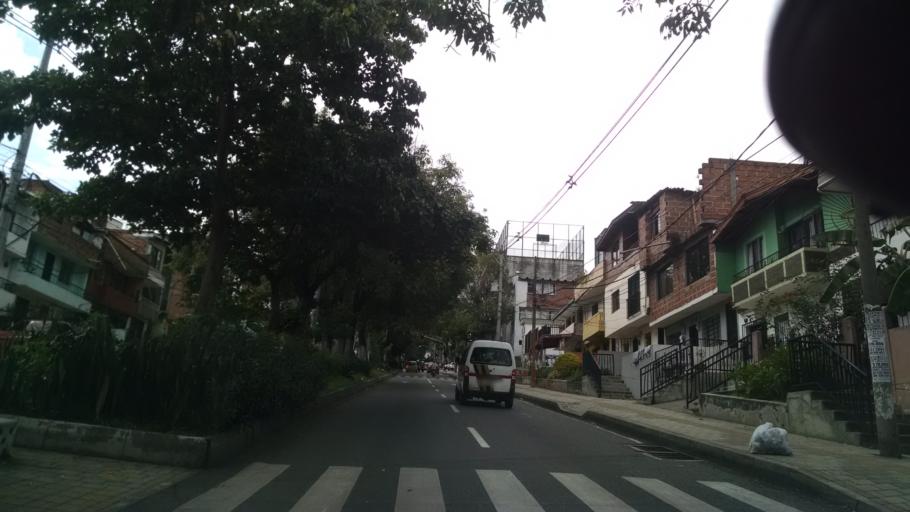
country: CO
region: Antioquia
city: Bello
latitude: 6.3009
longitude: -75.5712
